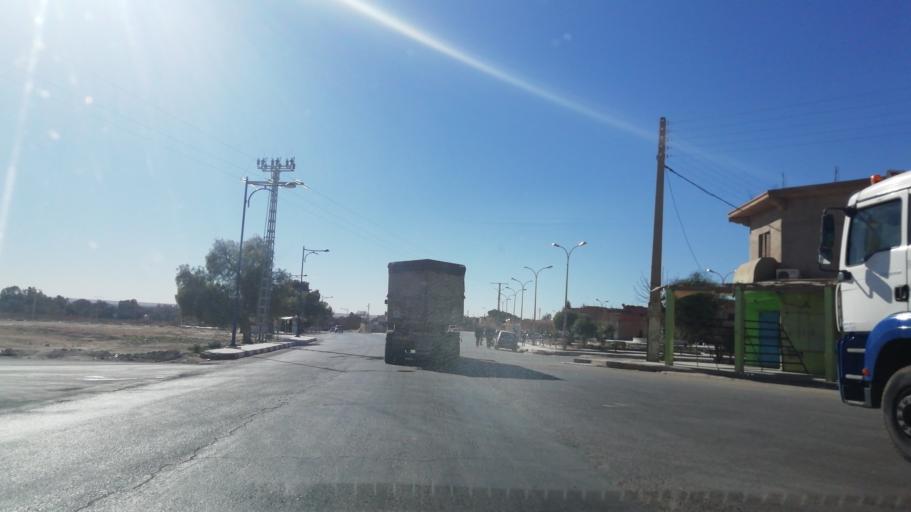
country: DZ
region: Saida
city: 'Ain el Hadjar
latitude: 34.1509
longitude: 0.0696
